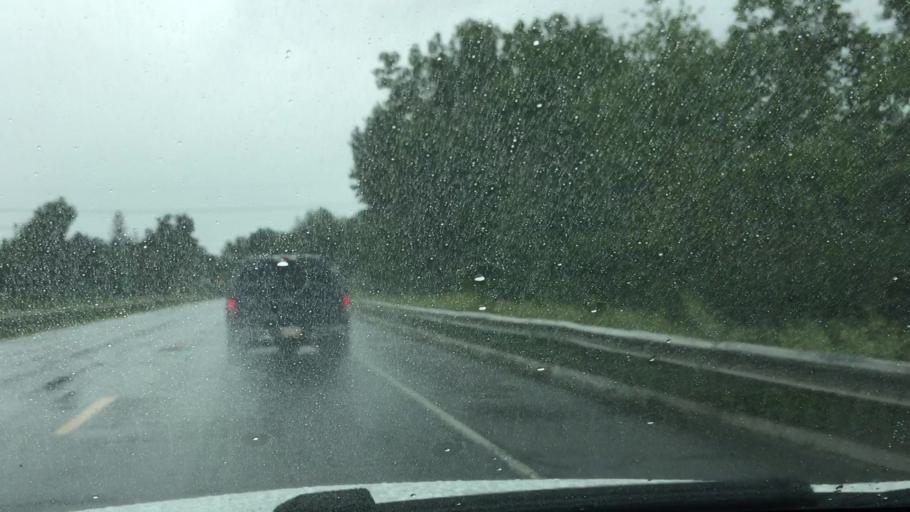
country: US
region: Massachusetts
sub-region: Berkshire County
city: Lanesborough
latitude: 42.5067
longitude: -73.2345
